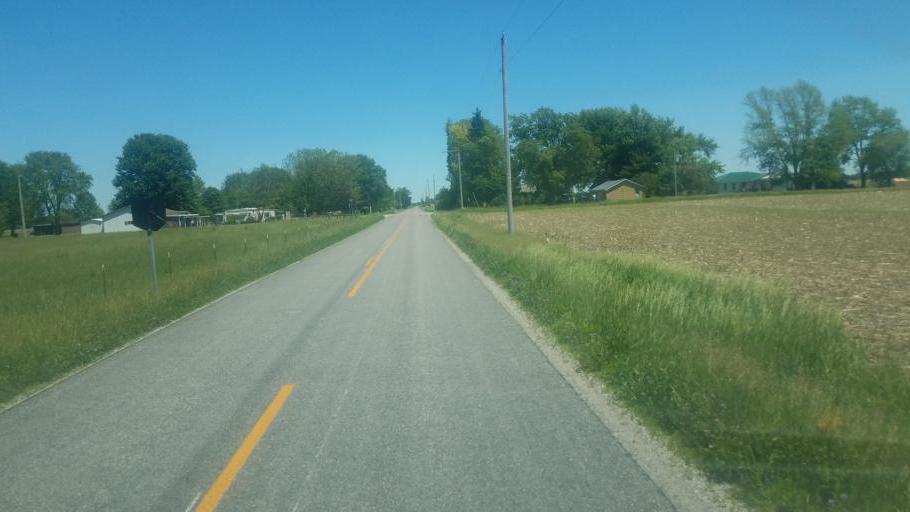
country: US
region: Ohio
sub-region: Shelby County
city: Sidney
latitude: 40.2125
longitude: -84.1356
